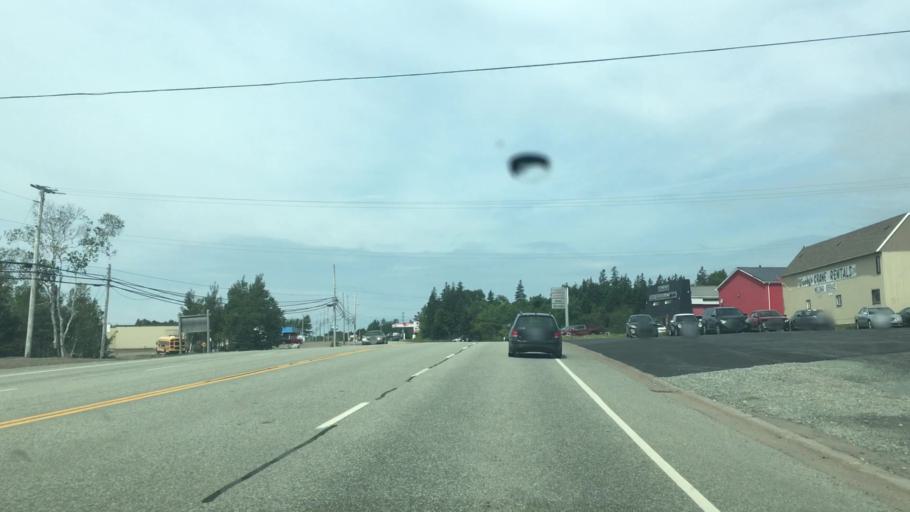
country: CA
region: Nova Scotia
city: Port Hawkesbury
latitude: 45.6386
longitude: -61.3838
